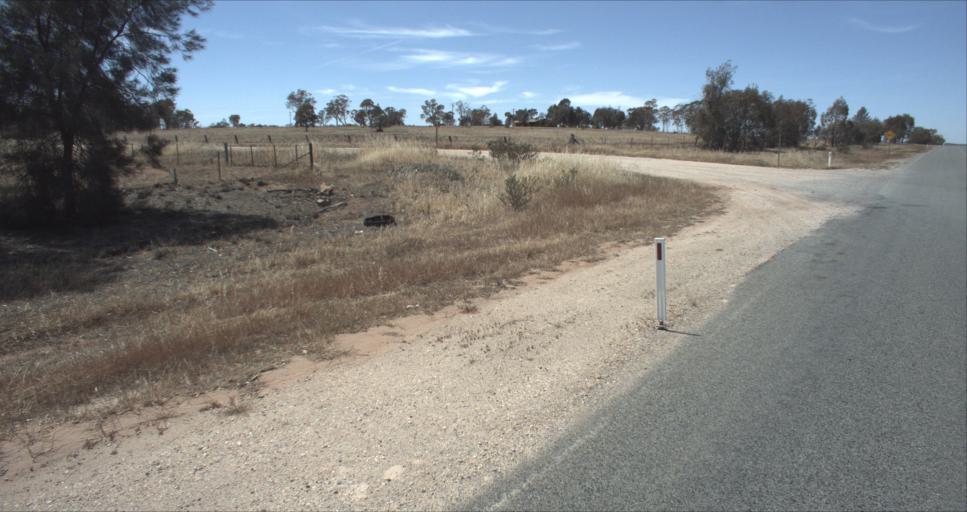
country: AU
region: New South Wales
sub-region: Leeton
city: Leeton
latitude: -34.6177
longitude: 146.4401
